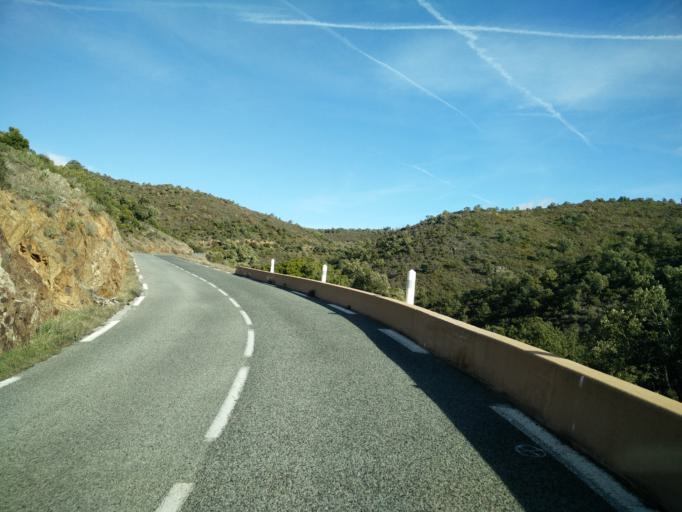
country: FR
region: Provence-Alpes-Cote d'Azur
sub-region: Departement du Var
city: Saint-Raphael
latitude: 43.4961
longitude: 6.7807
